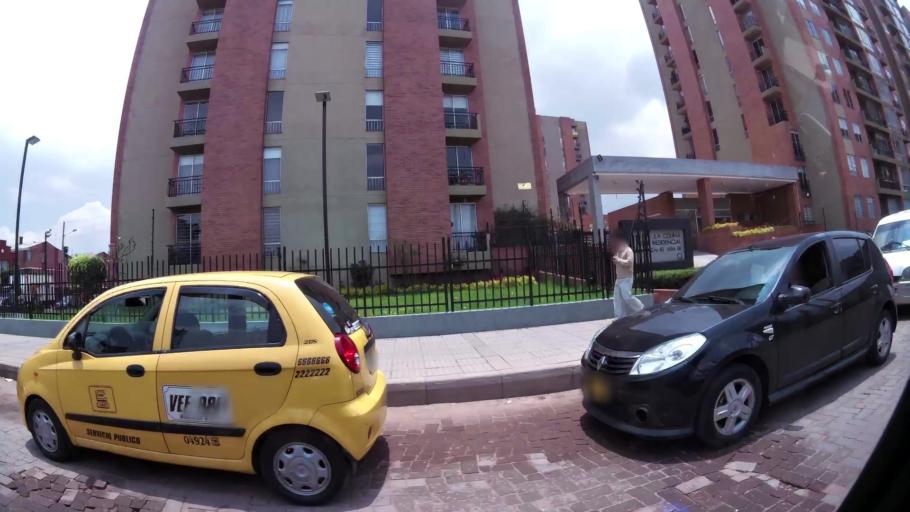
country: CO
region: Cundinamarca
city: Cota
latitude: 4.7498
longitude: -74.0616
